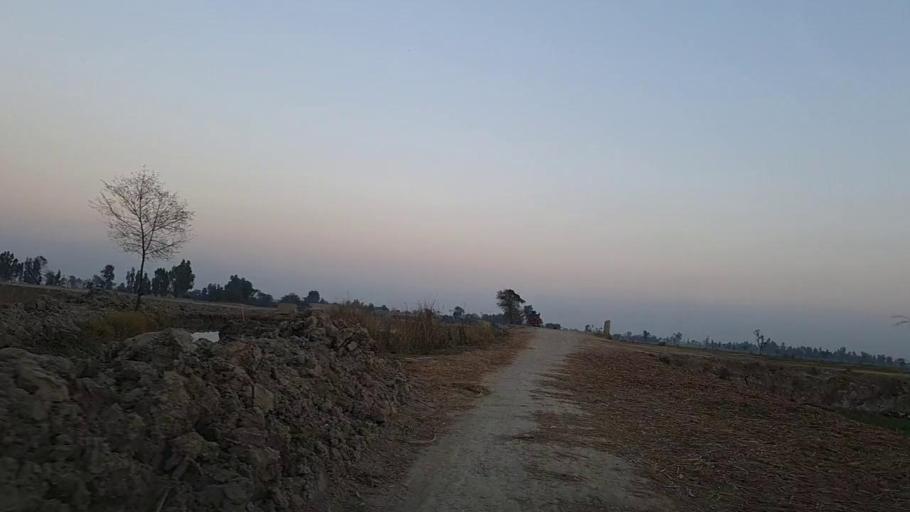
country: PK
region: Sindh
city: Naushahro Firoz
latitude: 26.7938
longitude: 68.0395
